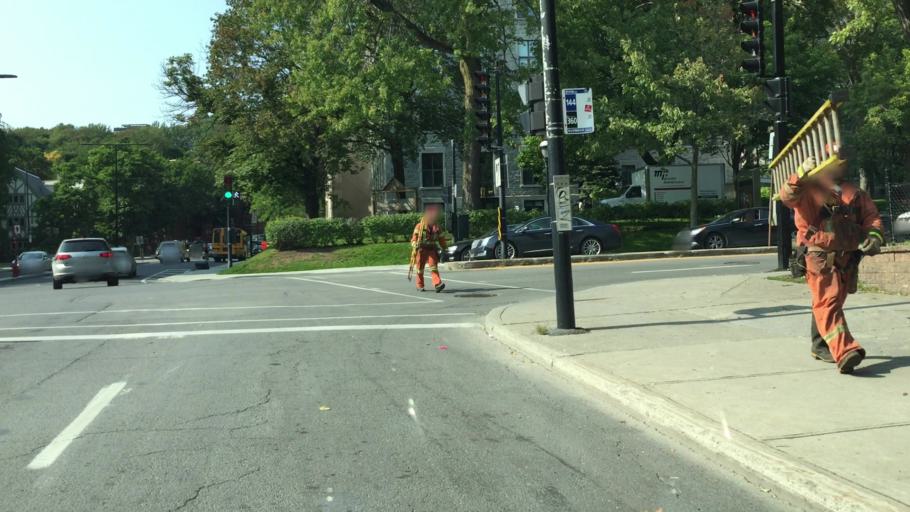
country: CA
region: Quebec
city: Westmount
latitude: 45.4913
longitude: -73.5876
